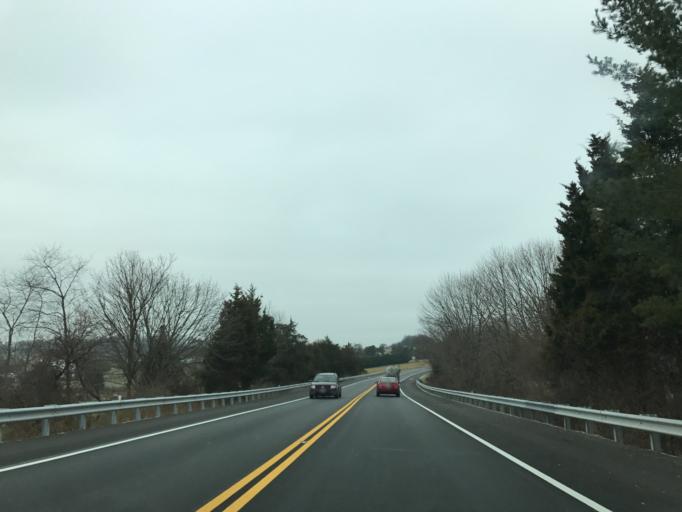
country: US
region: Maryland
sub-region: Carroll County
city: New Windsor
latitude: 39.6127
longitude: -77.0779
